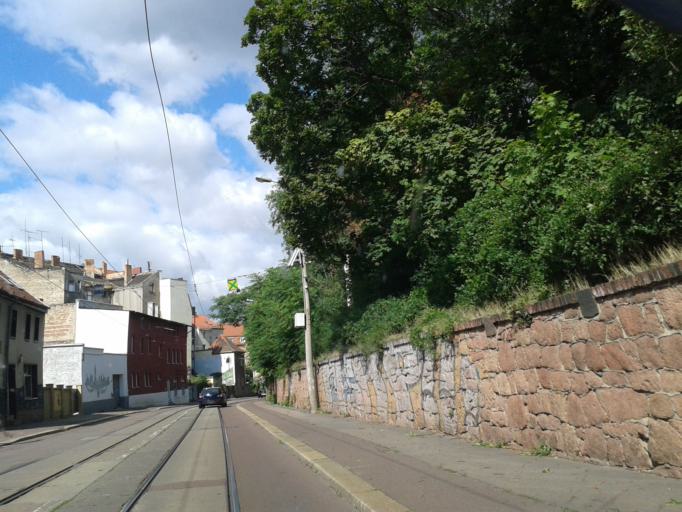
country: DE
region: Saxony-Anhalt
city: Halle (Saale)
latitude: 51.4998
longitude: 11.9604
